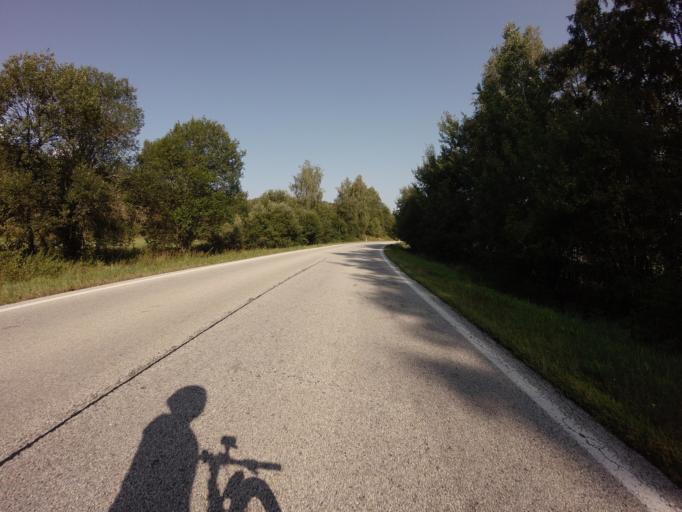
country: CZ
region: Jihocesky
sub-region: Okres Cesky Krumlov
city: Vyssi Brod
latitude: 48.6037
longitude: 14.3174
